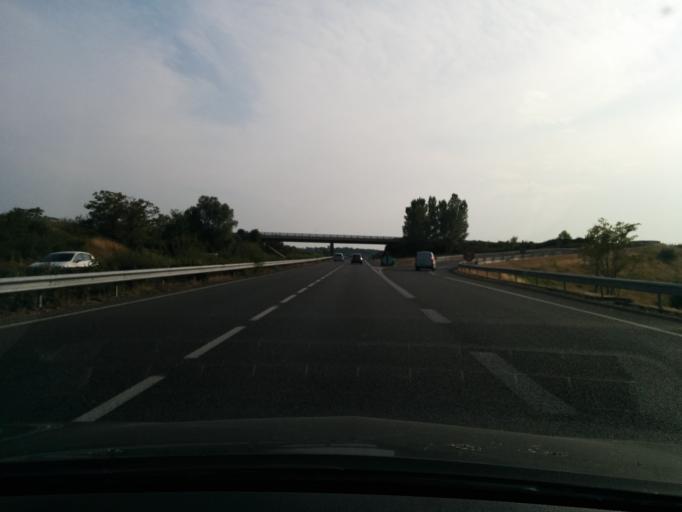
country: FR
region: Midi-Pyrenees
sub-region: Departement du Tarn
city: Saint-Sulpice-la-Pointe
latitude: 43.7600
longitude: 1.7118
